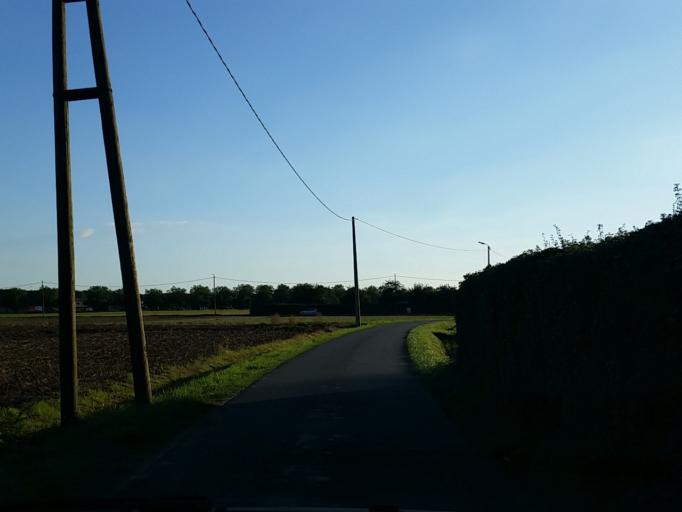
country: BE
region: Flanders
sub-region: Provincie Vlaams-Brabant
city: Steenokkerzeel
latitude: 50.9381
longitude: 4.4851
